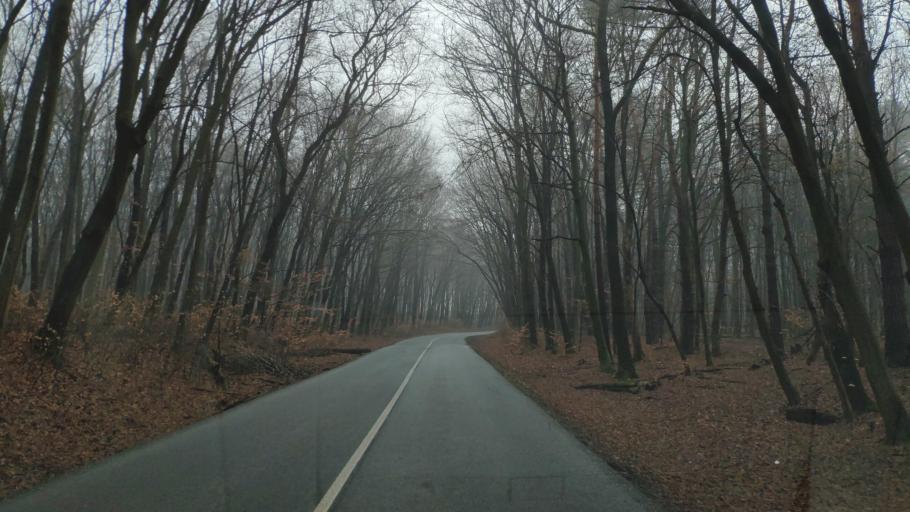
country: SK
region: Kosicky
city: Kosice
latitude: 48.7109
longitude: 21.3758
